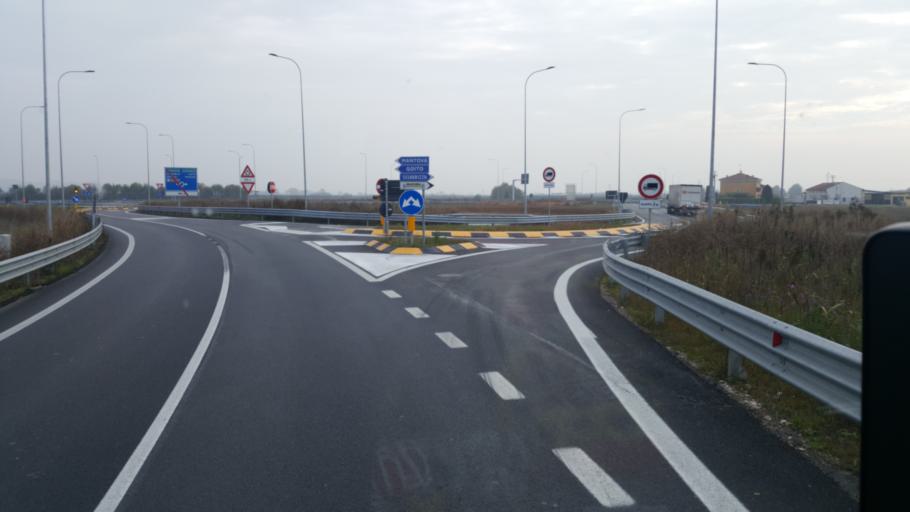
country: IT
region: Lombardy
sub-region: Provincia di Mantova
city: Guidizzolo
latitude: 45.3138
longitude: 10.5963
